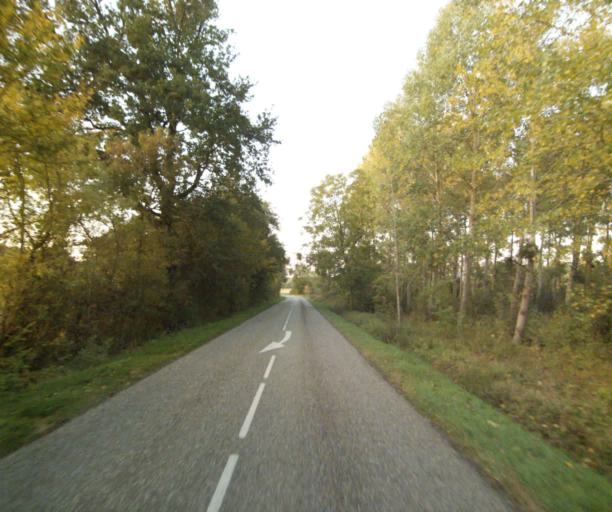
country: FR
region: Midi-Pyrenees
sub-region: Departement du Gers
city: Vic-Fezensac
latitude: 43.7852
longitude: 0.2591
